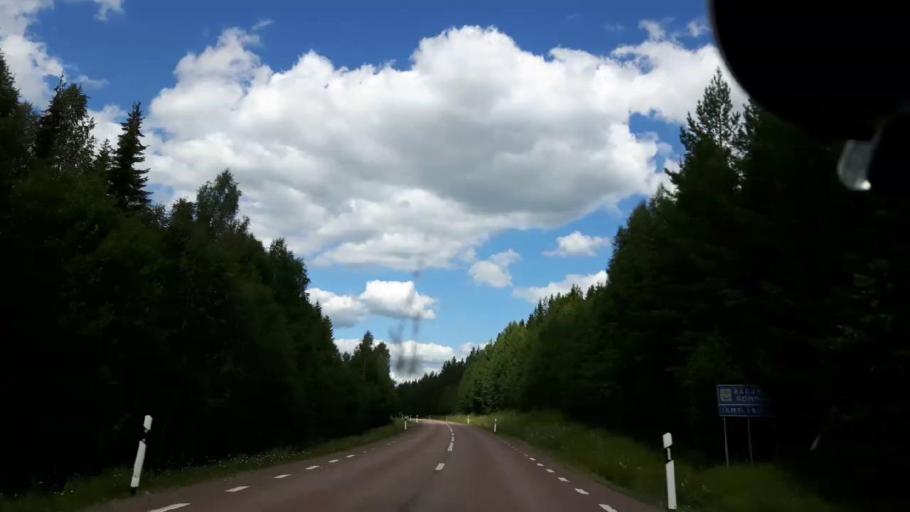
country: SE
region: Jaemtland
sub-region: Ragunda Kommun
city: Hammarstrand
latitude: 62.9208
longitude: 16.7038
